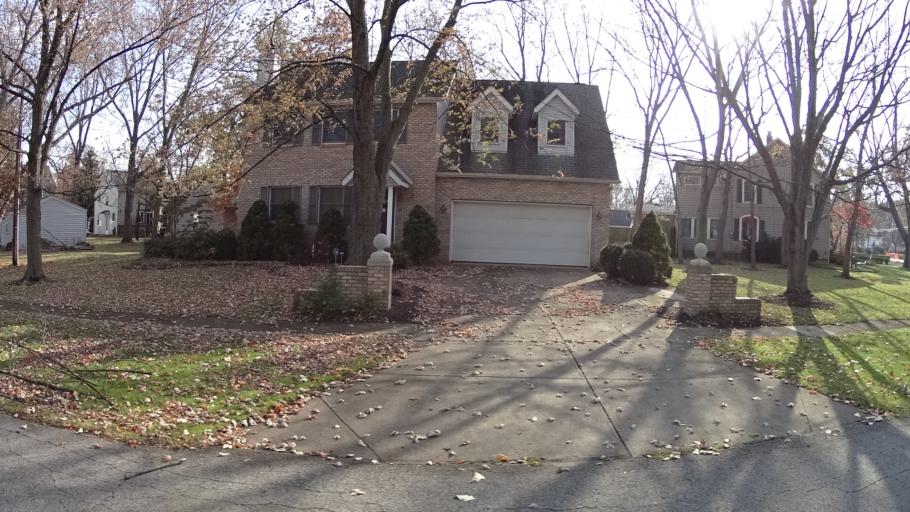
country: US
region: Ohio
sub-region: Lorain County
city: Elyria
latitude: 41.3898
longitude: -82.0920
